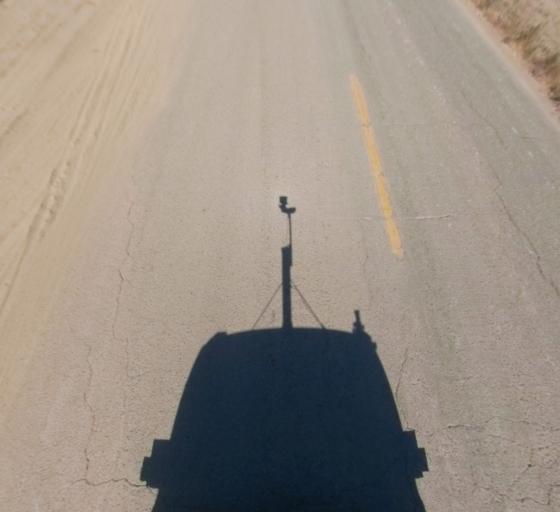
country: US
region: California
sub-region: Fresno County
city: Biola
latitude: 36.8658
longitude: -119.9498
